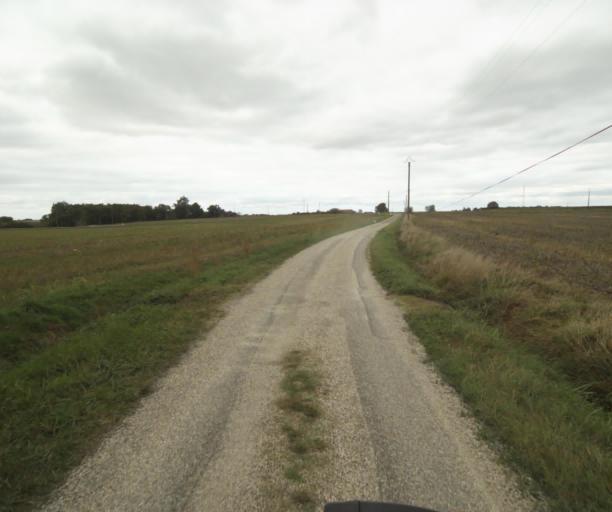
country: FR
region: Midi-Pyrenees
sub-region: Departement du Tarn-et-Garonne
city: Beaumont-de-Lomagne
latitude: 43.8631
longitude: 1.0693
